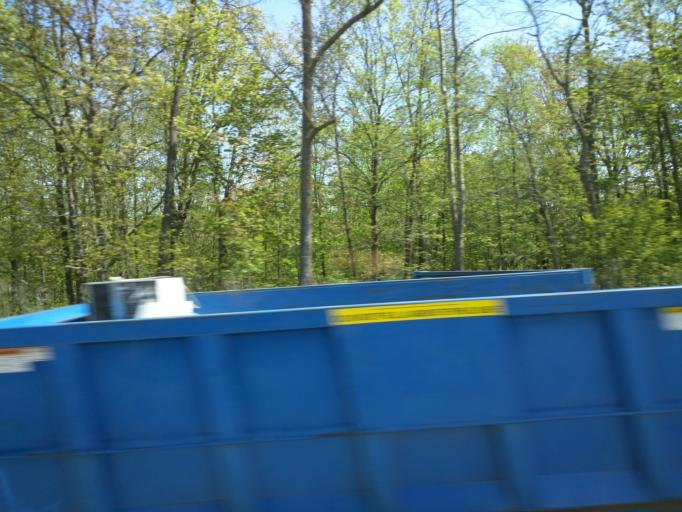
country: US
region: Wisconsin
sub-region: Monroe County
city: Cashton
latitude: 43.6667
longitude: -90.6472
